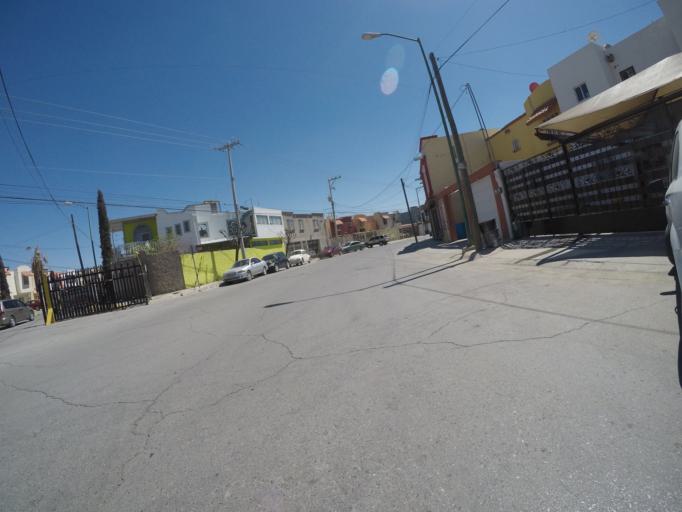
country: MX
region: Chihuahua
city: Ciudad Juarez
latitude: 31.6936
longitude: -106.4174
